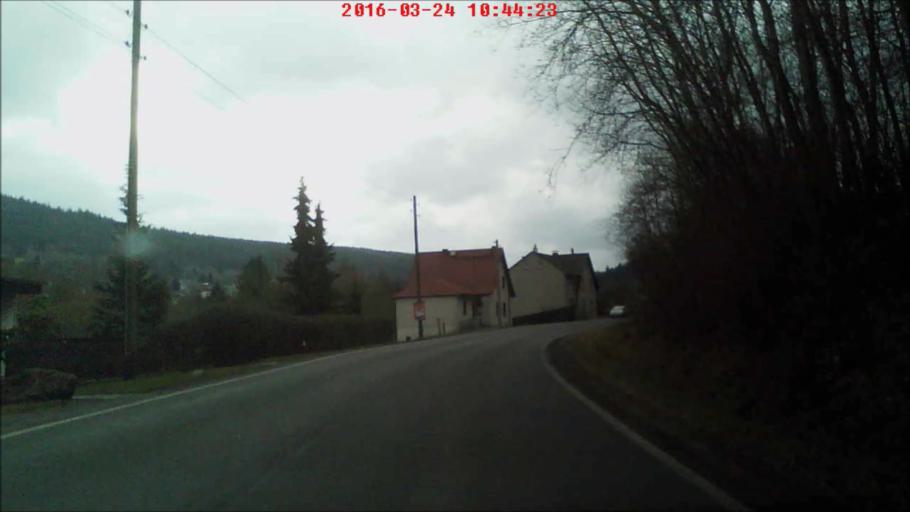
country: DE
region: Thuringia
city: Mohrenbach
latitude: 50.6327
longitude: 10.9962
